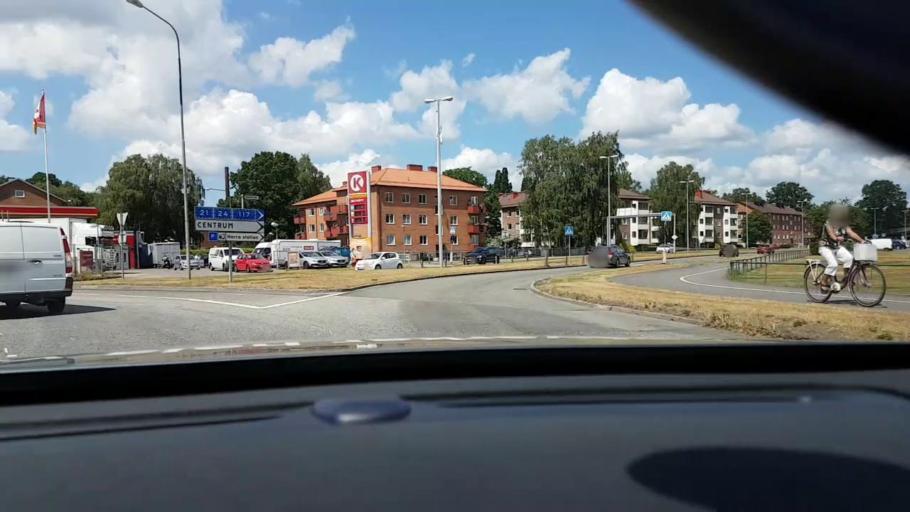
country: SE
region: Skane
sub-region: Hassleholms Kommun
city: Hassleholm
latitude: 56.1561
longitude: 13.7566
